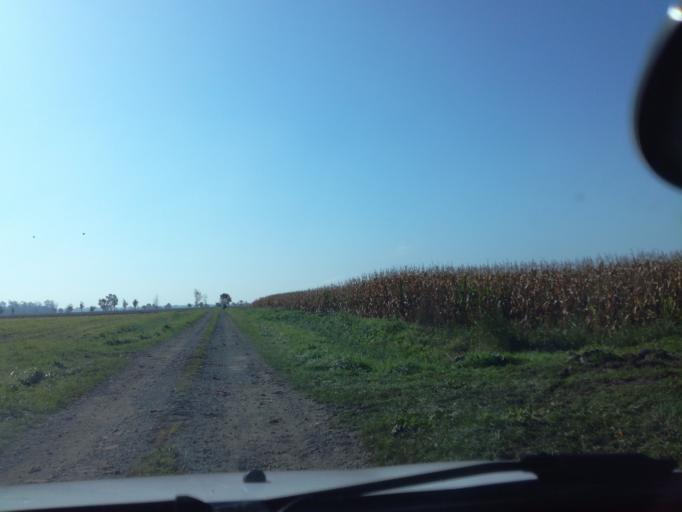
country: FR
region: Brittany
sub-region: Departement d'Ille-et-Vilaine
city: Cherrueix
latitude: 48.5914
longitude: -1.6857
